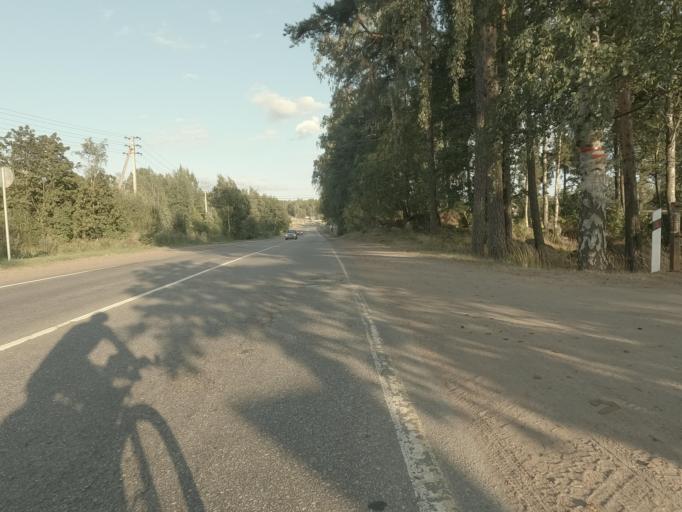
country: RU
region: Leningrad
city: Vyborg
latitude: 60.7262
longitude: 28.7609
